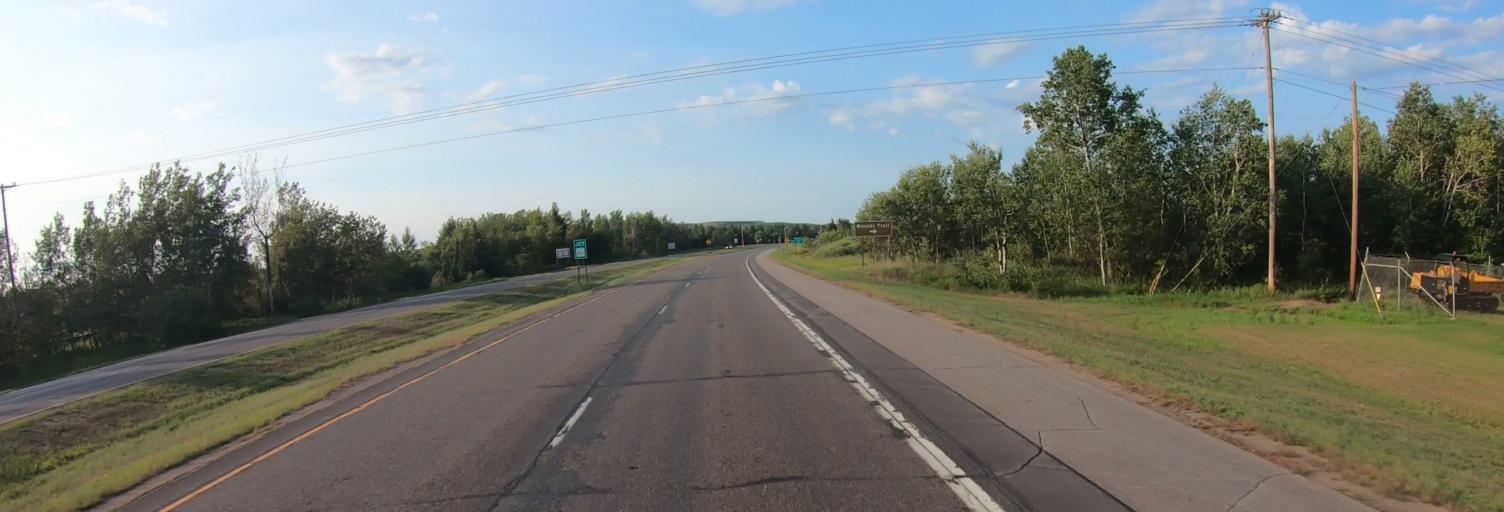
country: US
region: Minnesota
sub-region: Saint Louis County
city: Parkville
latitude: 47.5263
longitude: -92.5630
